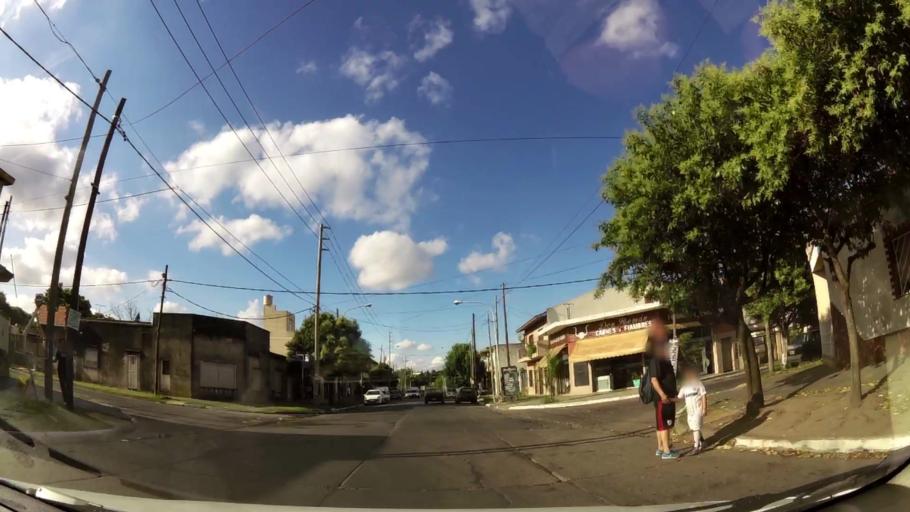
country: AR
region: Buenos Aires
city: San Justo
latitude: -34.6988
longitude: -58.5865
